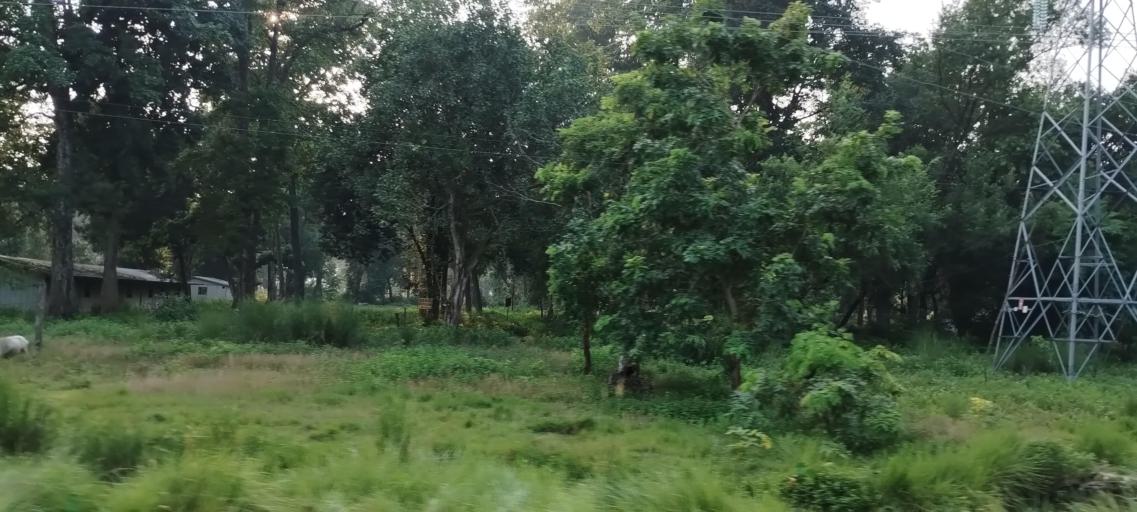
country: NP
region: Far Western
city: Tikapur
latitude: 28.5099
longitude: 81.3250
